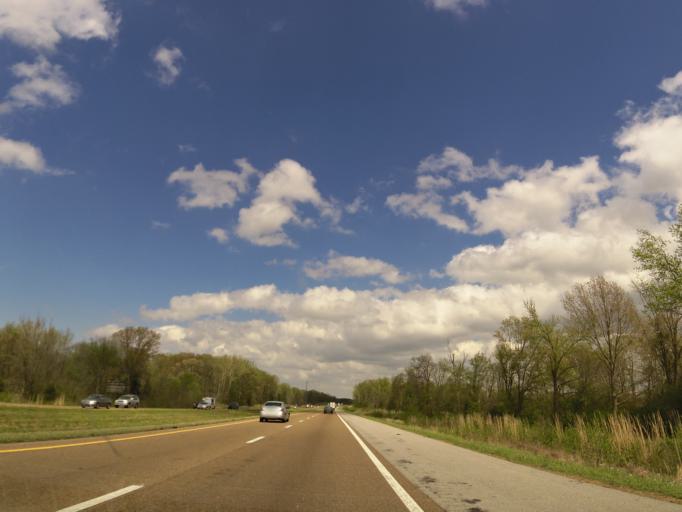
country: US
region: Tennessee
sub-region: Fayette County
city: Hickory Withe
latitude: 35.3257
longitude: -89.5632
